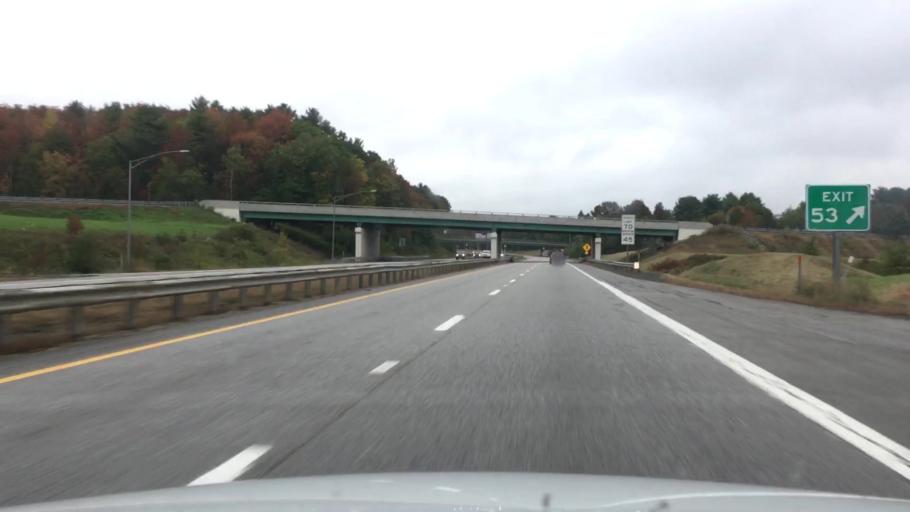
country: US
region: Maine
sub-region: Cumberland County
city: Falmouth
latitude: 43.7310
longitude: -70.3025
